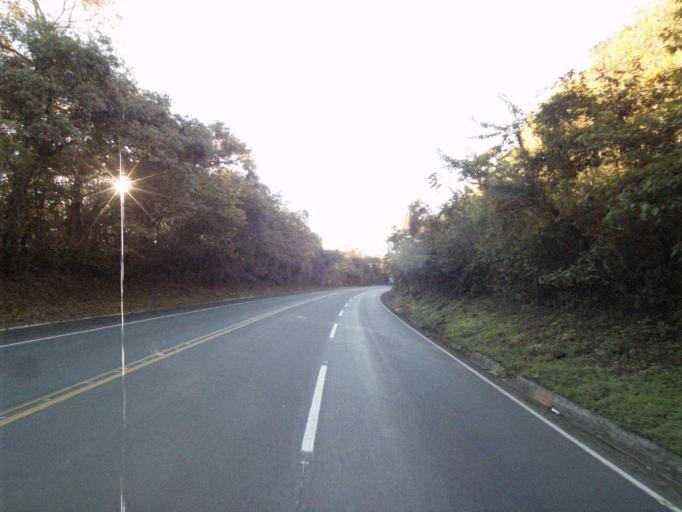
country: BR
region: Santa Catarina
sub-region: Chapeco
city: Chapeco
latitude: -26.9157
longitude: -52.8648
